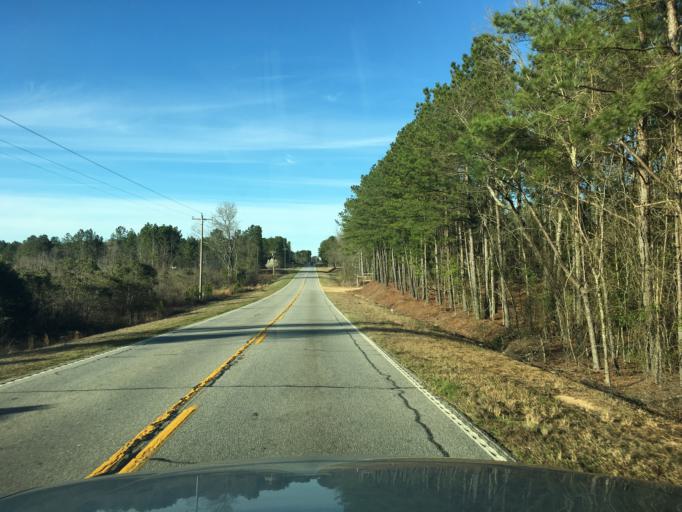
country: US
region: South Carolina
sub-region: Edgefield County
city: Johnston
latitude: 33.7546
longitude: -81.6430
